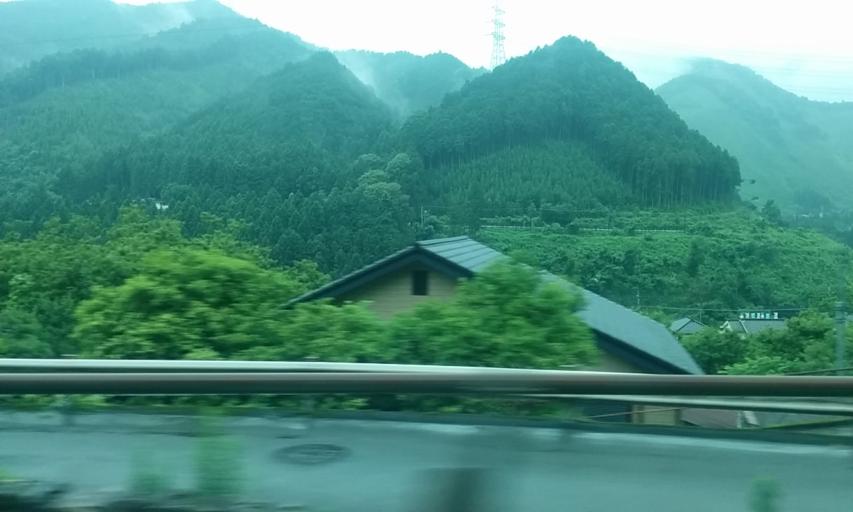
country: JP
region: Tokyo
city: Ome
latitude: 35.8067
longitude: 139.1903
